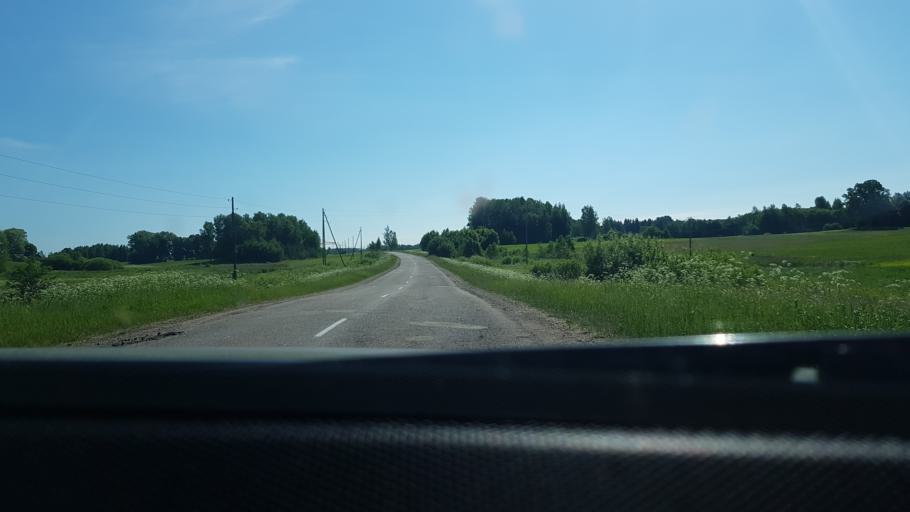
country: BY
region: Vitebsk
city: Braslaw
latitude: 55.8163
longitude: 26.8201
